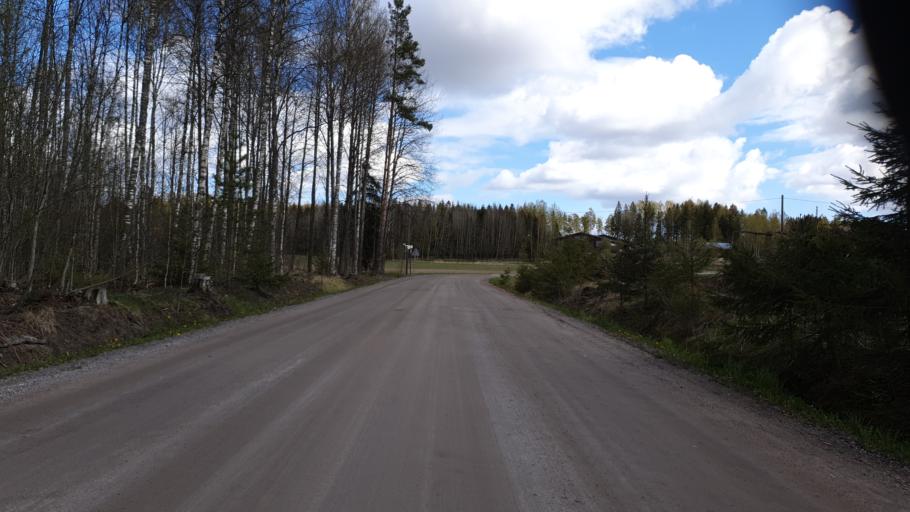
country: FI
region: Uusimaa
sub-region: Helsinki
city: Nurmijaervi
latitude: 60.3800
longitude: 24.8793
